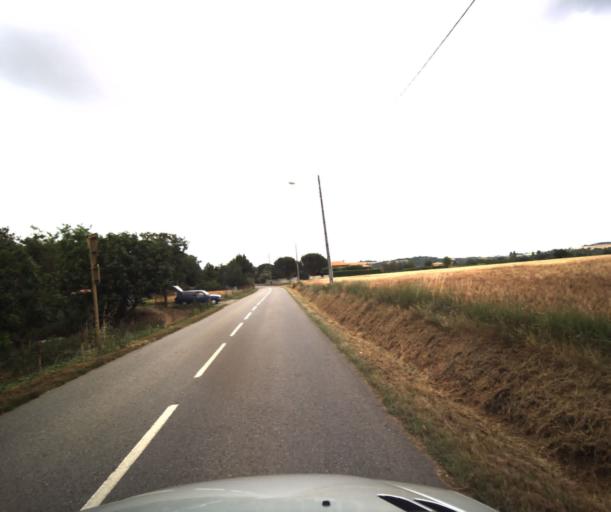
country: FR
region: Midi-Pyrenees
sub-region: Departement de la Haute-Garonne
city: Labarthe-sur-Leze
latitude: 43.4517
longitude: 1.4084
